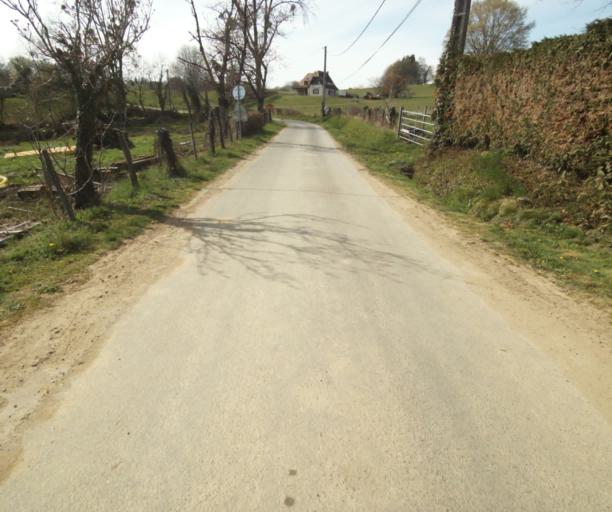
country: FR
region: Limousin
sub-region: Departement de la Correze
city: Naves
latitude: 45.3477
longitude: 1.7527
